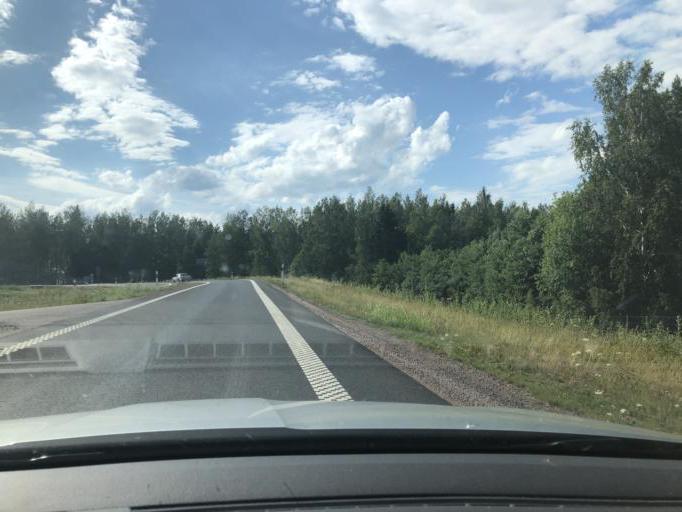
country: SE
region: OEstergoetland
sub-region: Vadstena Kommun
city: Herrestad
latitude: 58.2966
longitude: 14.9255
